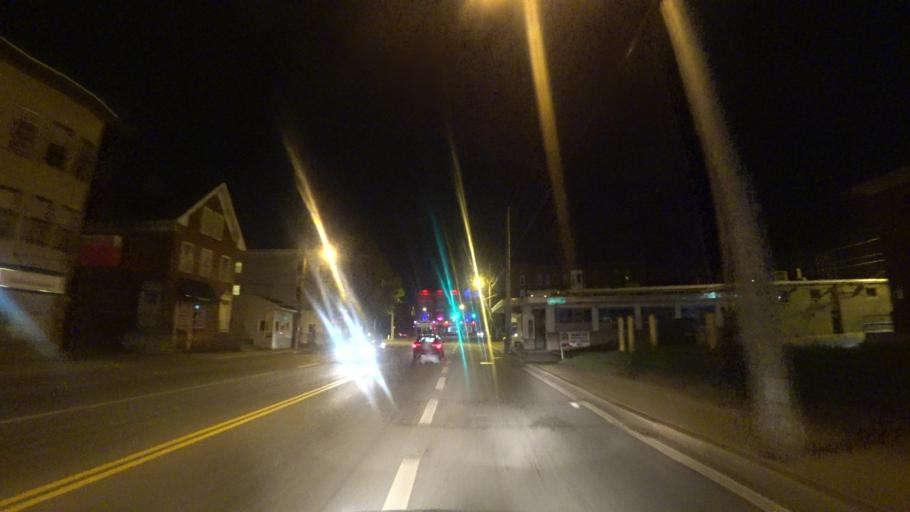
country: US
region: Massachusetts
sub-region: Essex County
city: Haverhill
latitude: 42.7783
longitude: -71.0904
